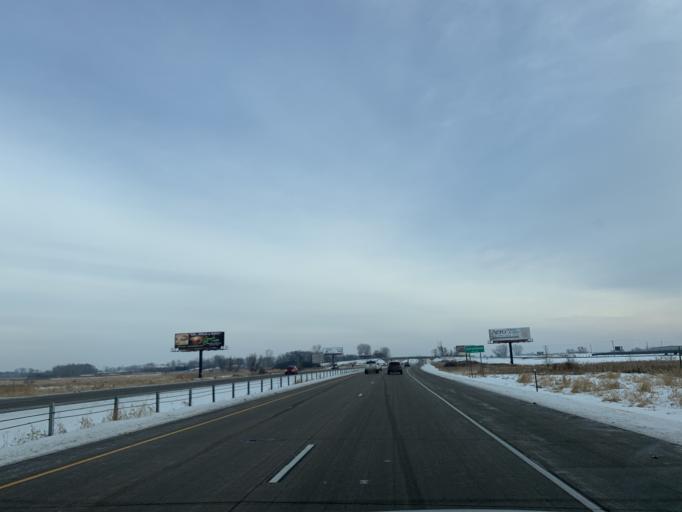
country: US
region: Minnesota
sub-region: Anoka County
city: Centerville
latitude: 45.2111
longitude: -93.0389
